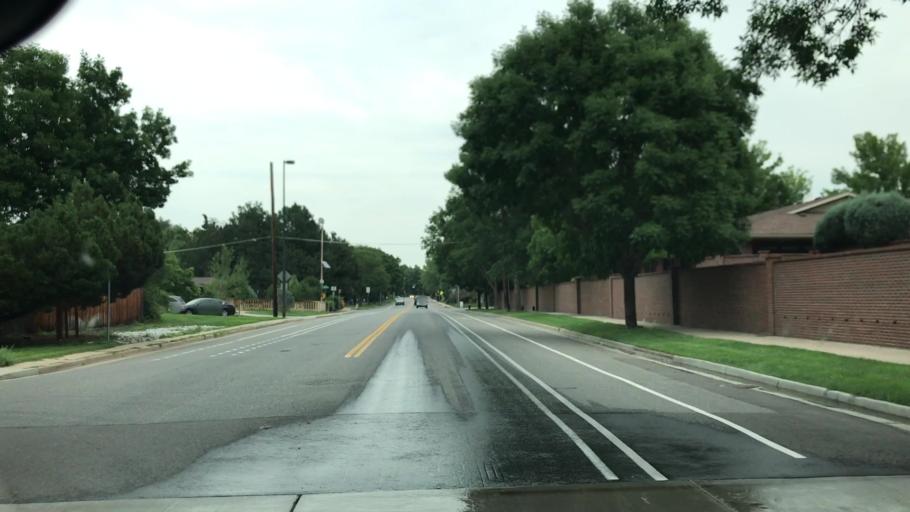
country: US
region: Colorado
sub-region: Arapahoe County
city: Cherry Hills Village
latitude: 39.6676
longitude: -104.9566
